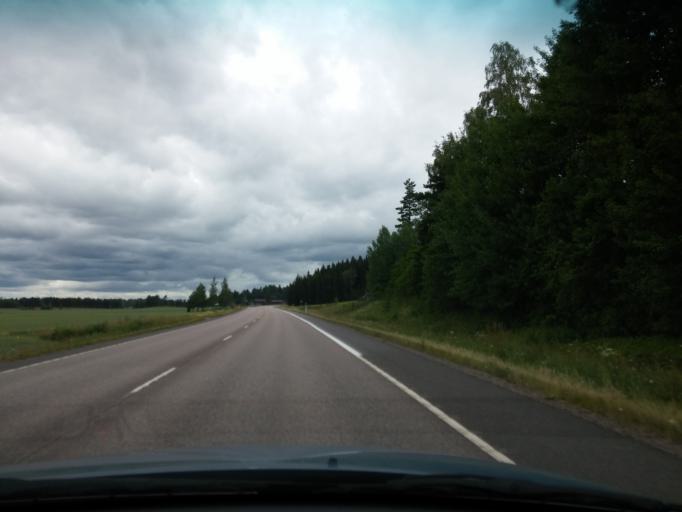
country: FI
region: Uusimaa
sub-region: Porvoo
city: Askola
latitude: 60.4837
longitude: 25.5616
